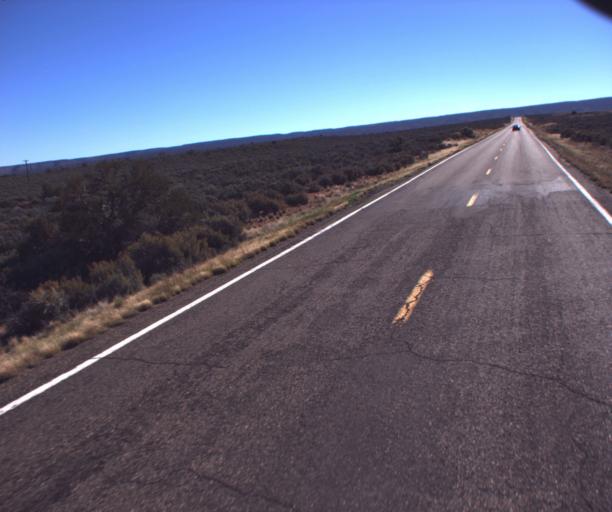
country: US
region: Arizona
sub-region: Coconino County
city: Fredonia
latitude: 36.8775
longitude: -112.3347
